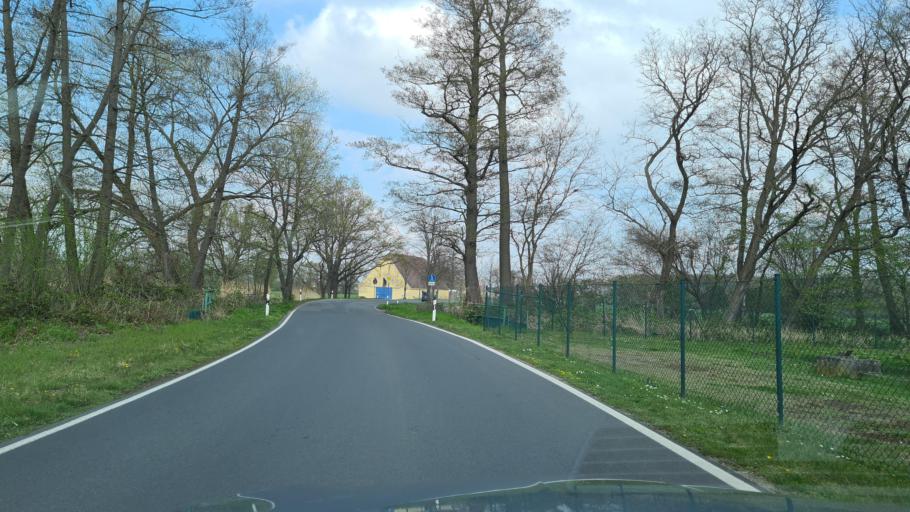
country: DE
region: Saxony
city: Wulknitz
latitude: 51.3844
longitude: 13.4323
